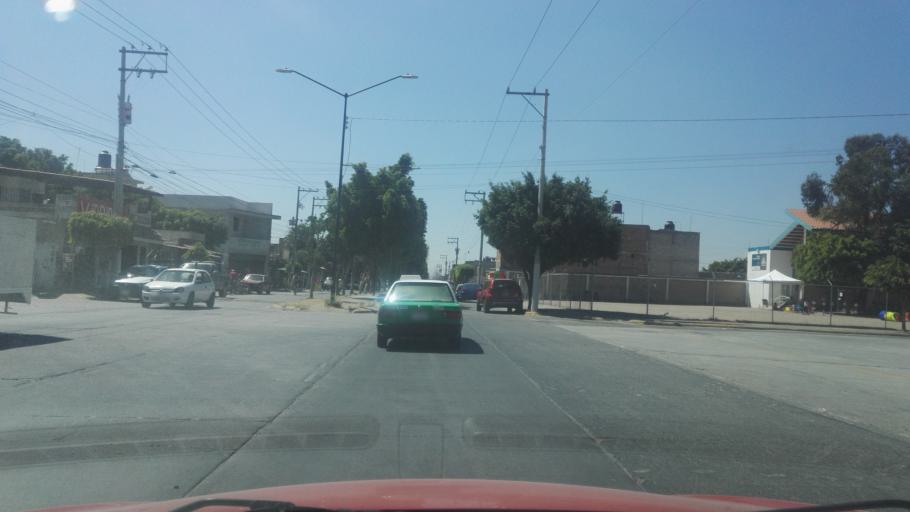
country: MX
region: Guanajuato
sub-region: Leon
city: Fraccionamiento Paraiso Real
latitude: 21.1029
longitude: -101.5854
